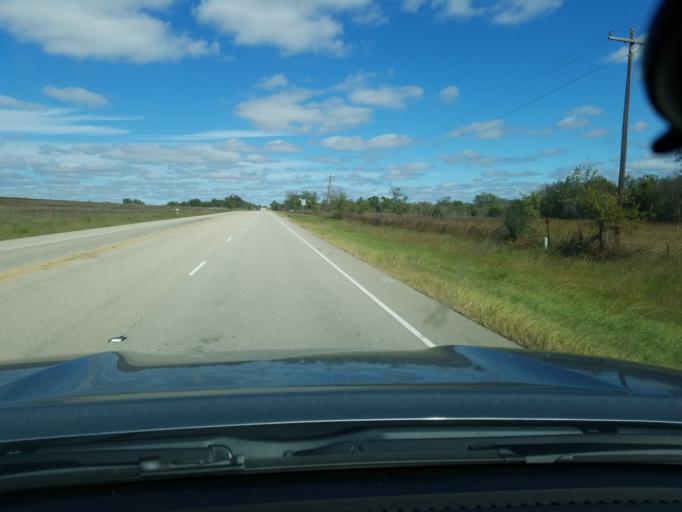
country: US
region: Texas
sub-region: Hamilton County
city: Hamilton
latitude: 31.6480
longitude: -98.1470
